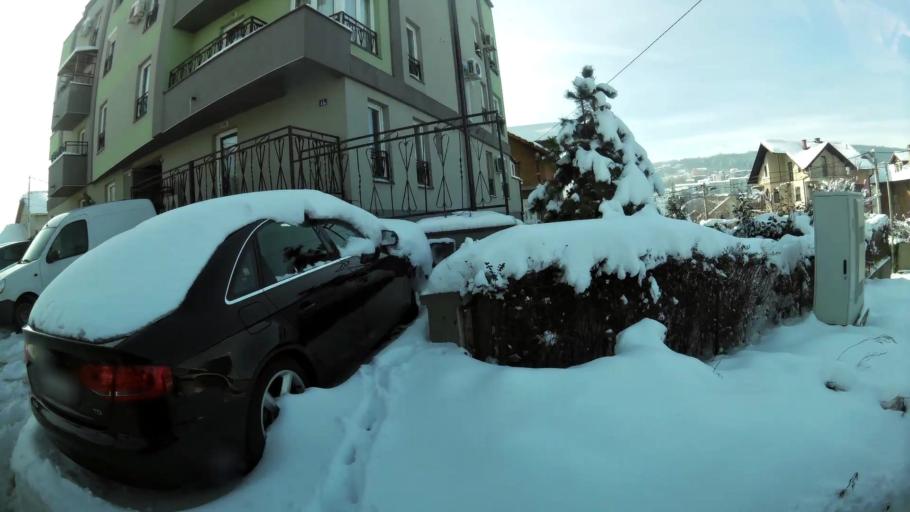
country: RS
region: Central Serbia
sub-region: Belgrade
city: Palilula
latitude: 44.8004
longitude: 20.5296
